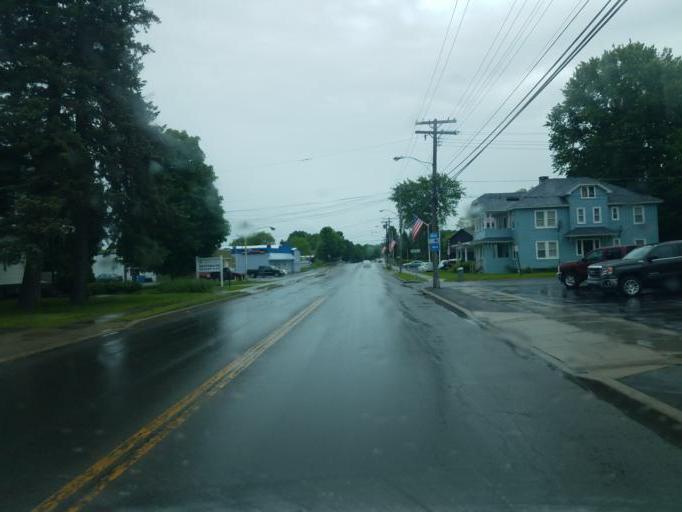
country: US
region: New York
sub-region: Herkimer County
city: Mohawk
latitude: 43.0100
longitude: -75.0135
